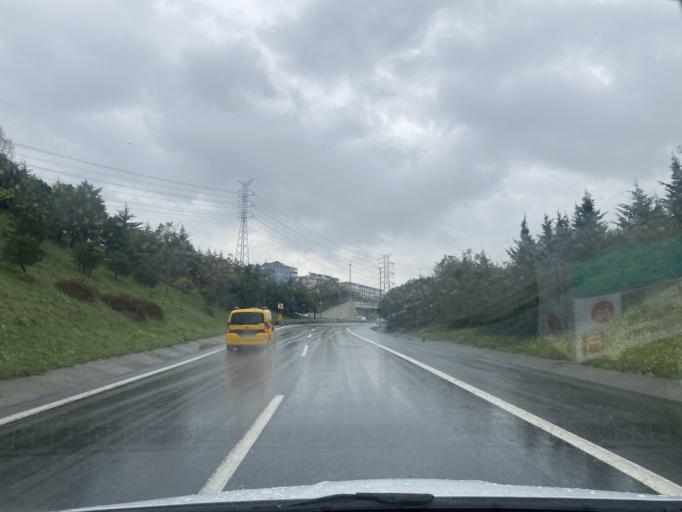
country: TR
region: Istanbul
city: Sisli
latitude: 41.0724
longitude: 28.9581
